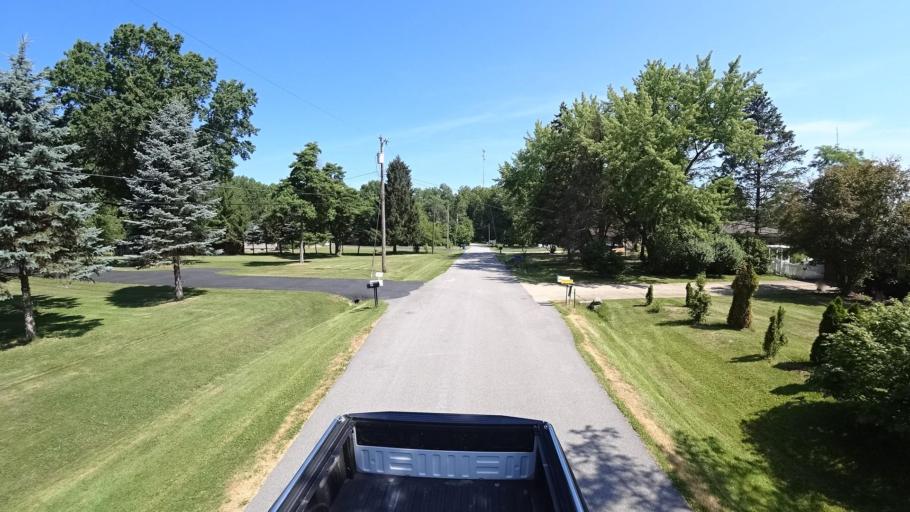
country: US
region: Indiana
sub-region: Porter County
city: Chesterton
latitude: 41.6306
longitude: -87.0565
